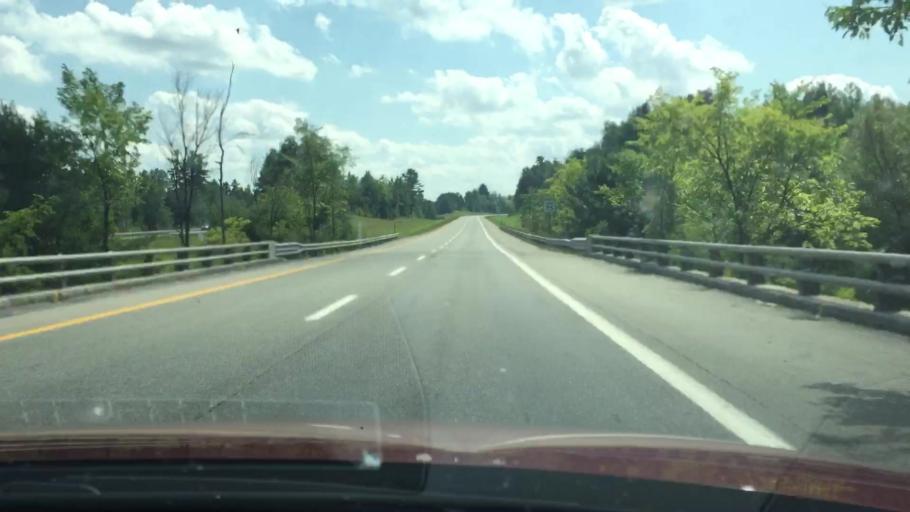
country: US
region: Maine
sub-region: Penobscot County
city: Lincoln
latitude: 45.3634
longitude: -68.6060
